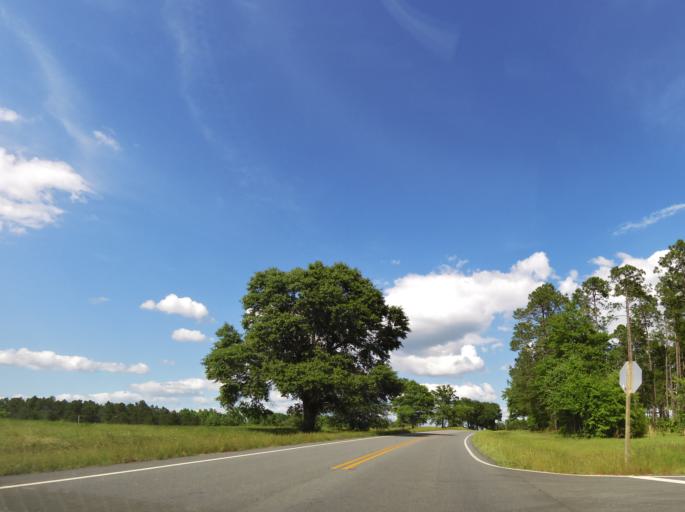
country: US
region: Georgia
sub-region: Treutlen County
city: Soperton
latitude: 32.3853
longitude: -82.5847
